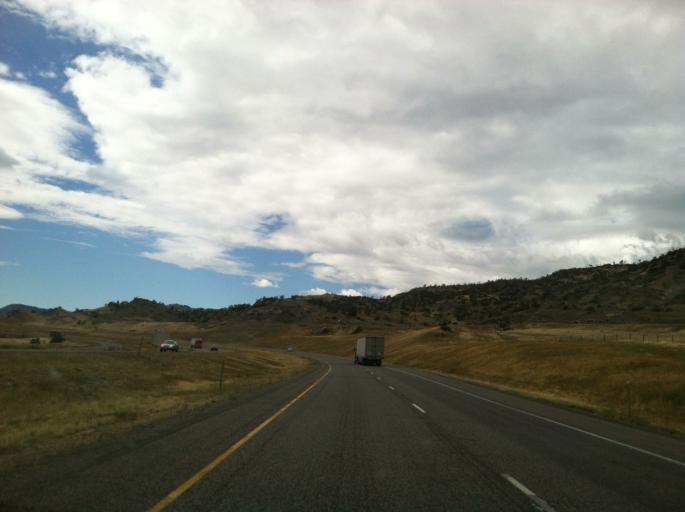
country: US
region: Montana
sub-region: Park County
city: Livingston
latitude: 45.6613
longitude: -110.6390
